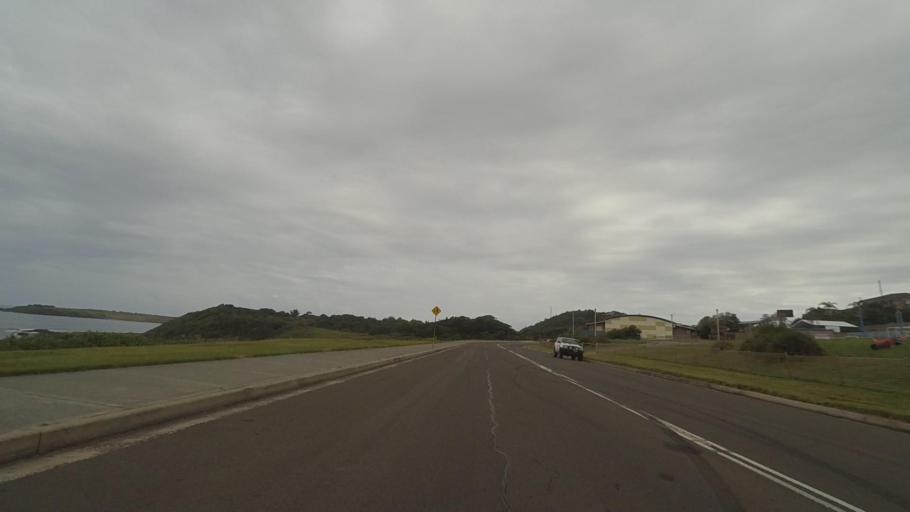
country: AU
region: New South Wales
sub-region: Wollongong
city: Port Kembla
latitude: -34.4853
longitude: 150.9150
